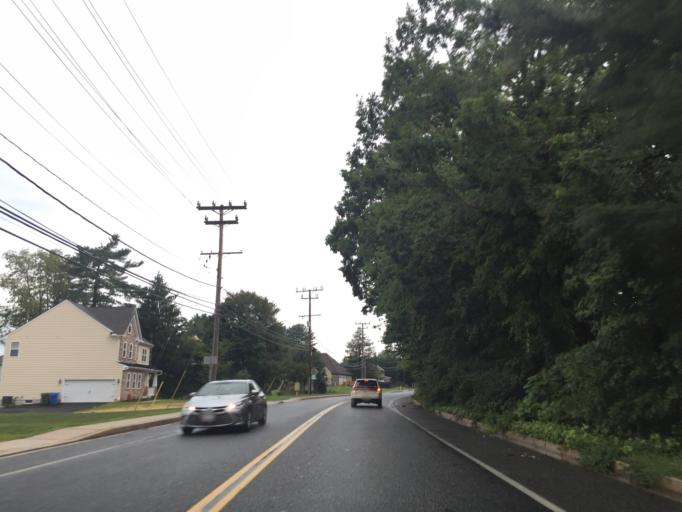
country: US
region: Maryland
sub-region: Harford County
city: Bel Air South
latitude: 39.4749
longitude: -76.3023
